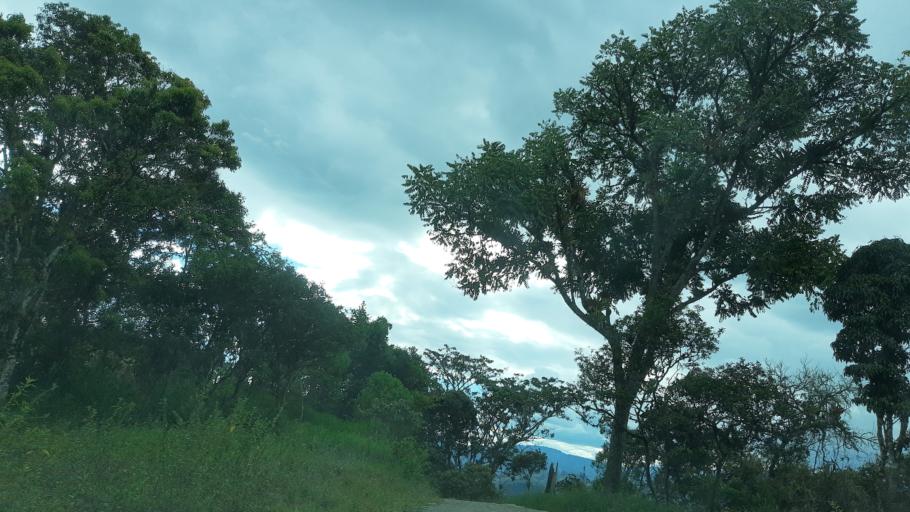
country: CO
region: Boyaca
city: Garagoa
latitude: 5.0220
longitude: -73.3282
